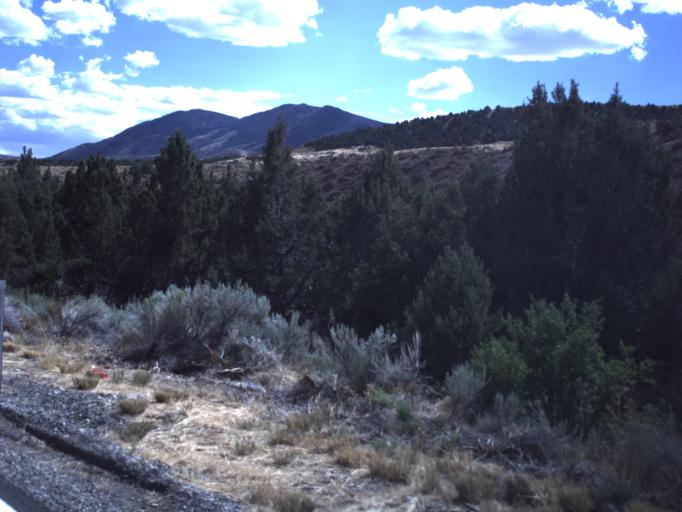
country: US
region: Utah
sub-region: Tooele County
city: Grantsville
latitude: 40.3403
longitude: -112.5366
